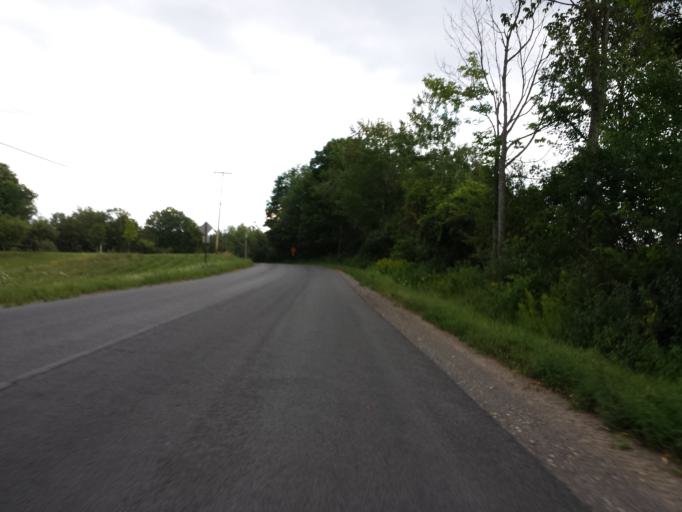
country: US
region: New York
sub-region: St. Lawrence County
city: Potsdam
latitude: 44.6854
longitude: -75.0090
